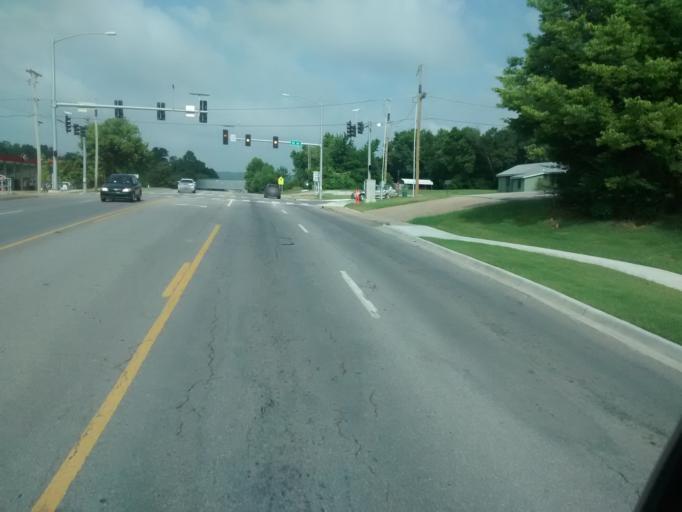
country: US
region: Arkansas
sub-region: Washington County
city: Fayetteville
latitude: 36.0567
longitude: -94.1693
